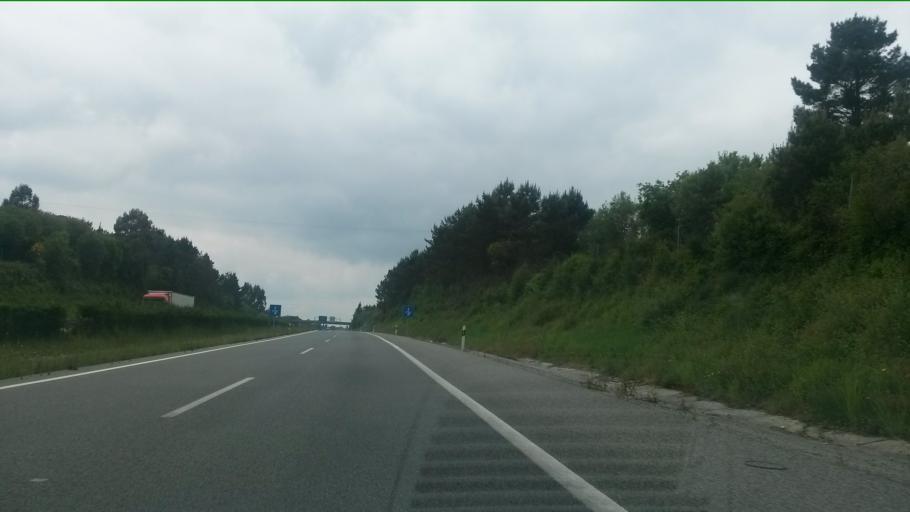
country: ES
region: Galicia
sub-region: Provincia de Lugo
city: Guitiriz
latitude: 43.1916
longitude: -7.9410
